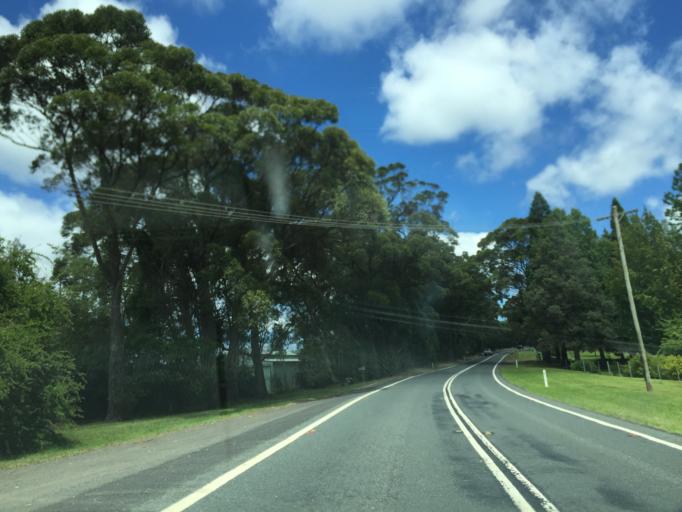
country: AU
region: New South Wales
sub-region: Blue Mountains Municipality
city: Hazelbrook
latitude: -33.5170
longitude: 150.4855
